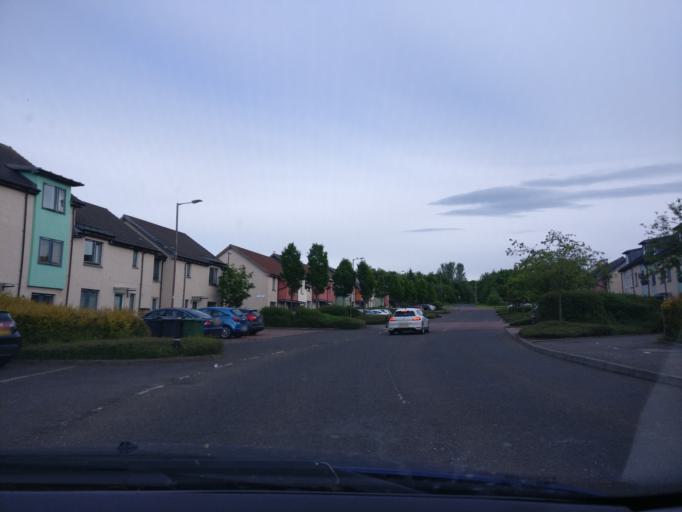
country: GB
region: Scotland
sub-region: West Lothian
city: Seafield
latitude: 55.9313
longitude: -3.1404
